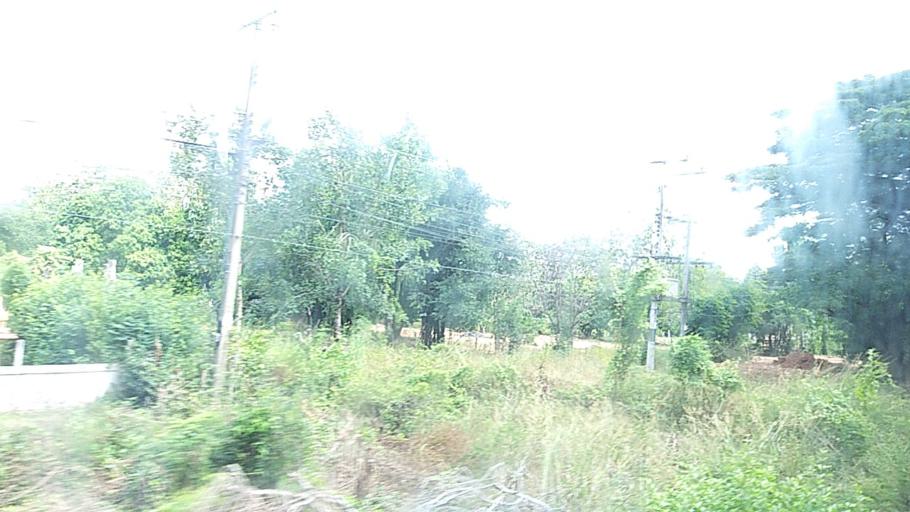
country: TH
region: Maha Sarakham
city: Chiang Yuen
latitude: 16.3437
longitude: 103.1310
